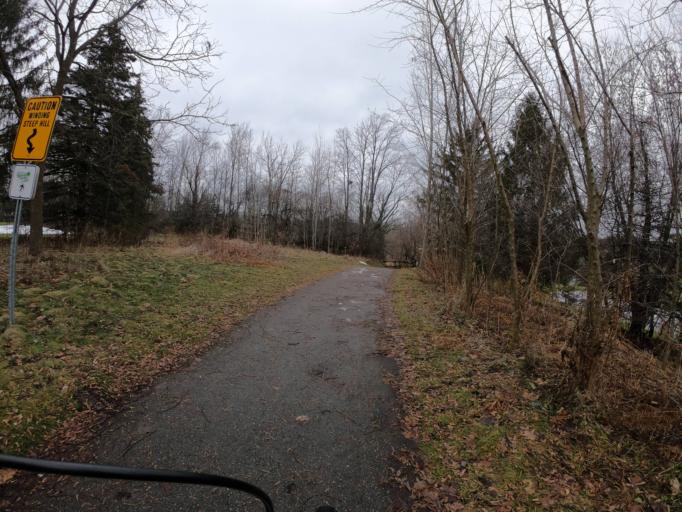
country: CA
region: Ontario
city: Cambridge
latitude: 43.3951
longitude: -80.3966
